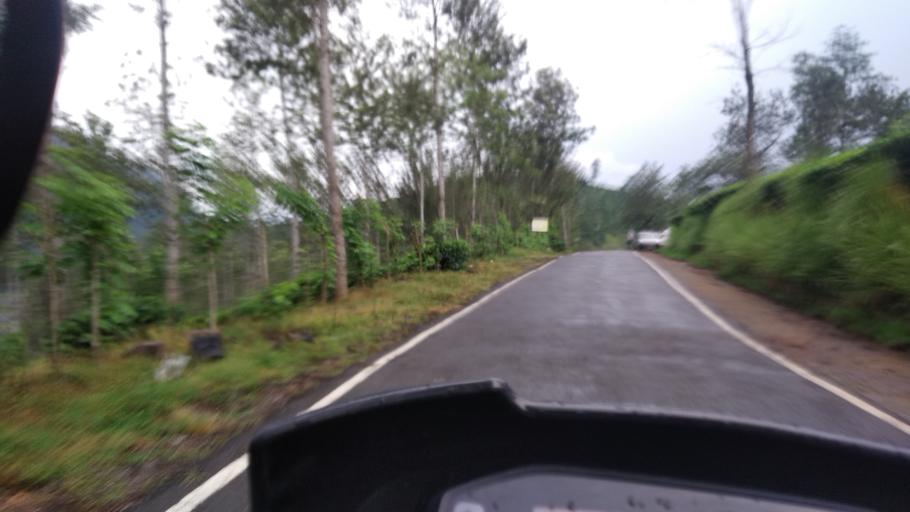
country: IN
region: Tamil Nadu
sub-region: Theni
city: Gudalur
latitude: 9.5682
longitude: 77.0839
